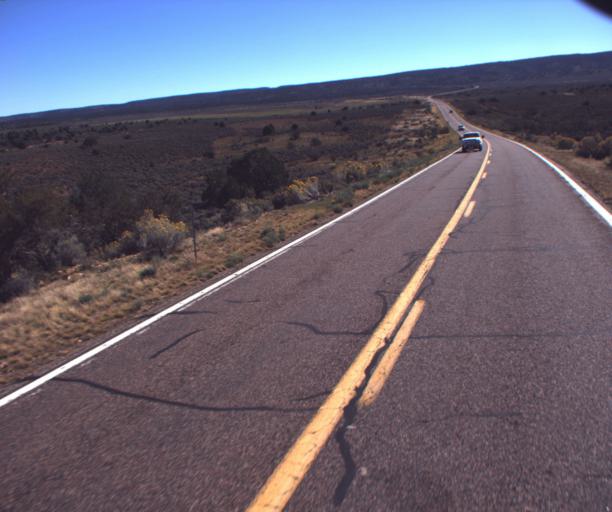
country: US
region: Arizona
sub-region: Coconino County
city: Fredonia
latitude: 36.8586
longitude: -112.3077
